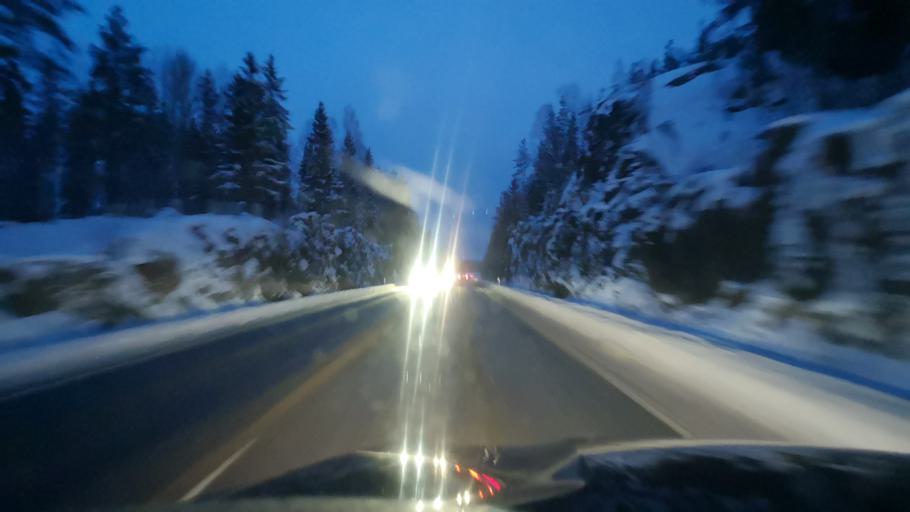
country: FI
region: Varsinais-Suomi
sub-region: Loimaa
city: Loimaa
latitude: 60.8751
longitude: 23.0682
